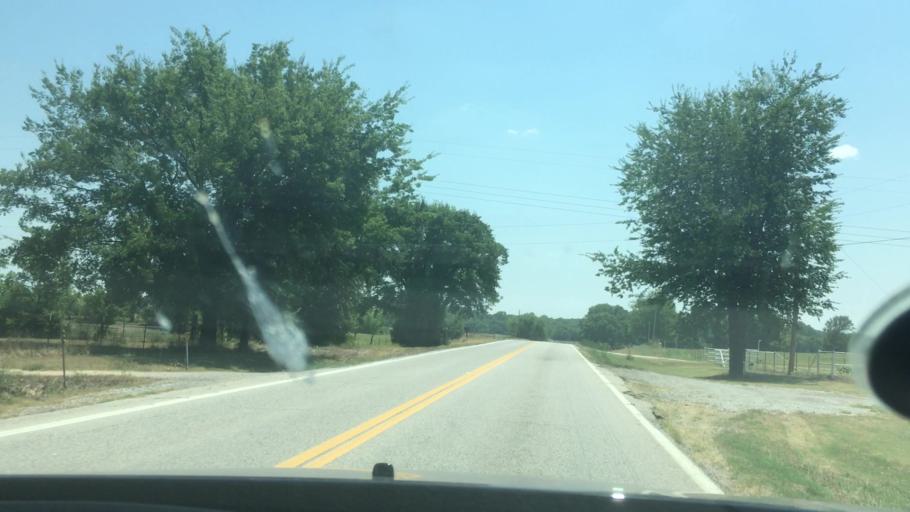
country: US
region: Oklahoma
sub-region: Bryan County
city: Durant
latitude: 34.0998
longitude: -96.3644
